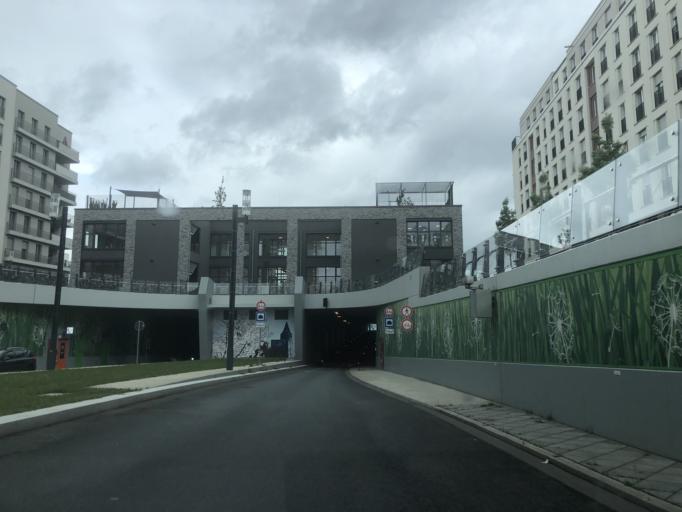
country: DE
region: Hesse
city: Niederrad
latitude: 50.1075
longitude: 8.6273
